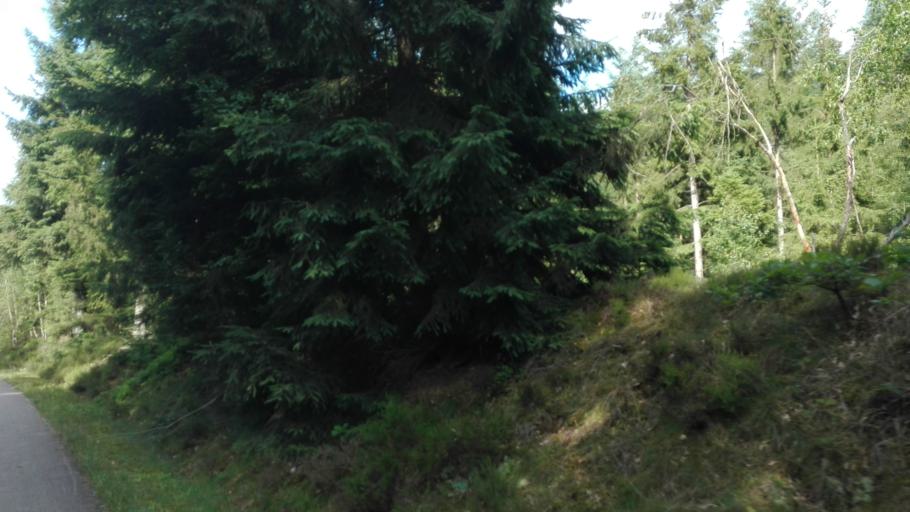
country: DK
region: Central Jutland
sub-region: Silkeborg Kommune
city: Virklund
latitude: 56.0422
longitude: 9.4716
